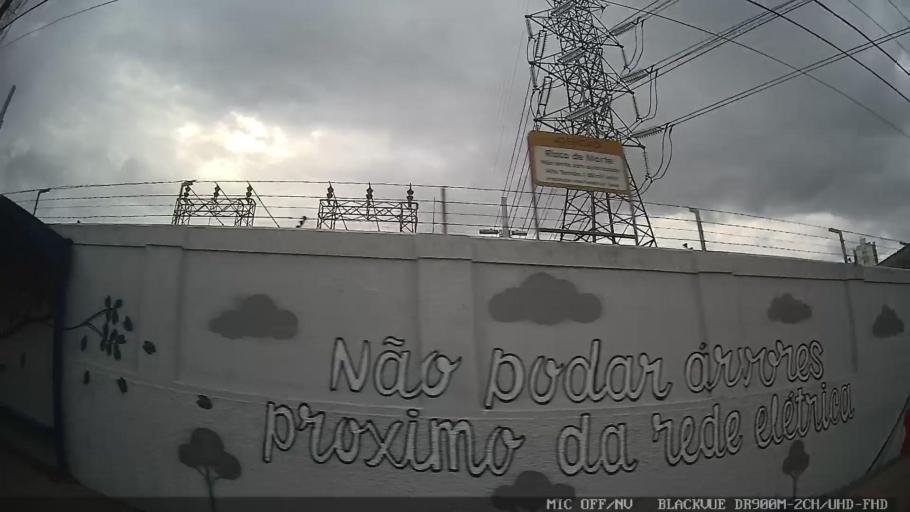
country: BR
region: Sao Paulo
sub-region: Mogi das Cruzes
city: Mogi das Cruzes
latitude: -23.5294
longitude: -46.1937
